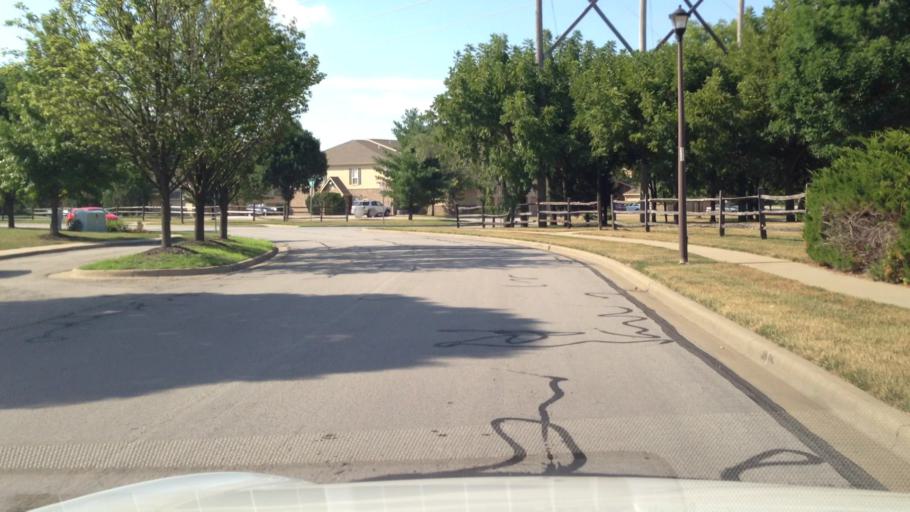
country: US
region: Kansas
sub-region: Johnson County
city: Lenexa
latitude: 38.9179
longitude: -94.7550
